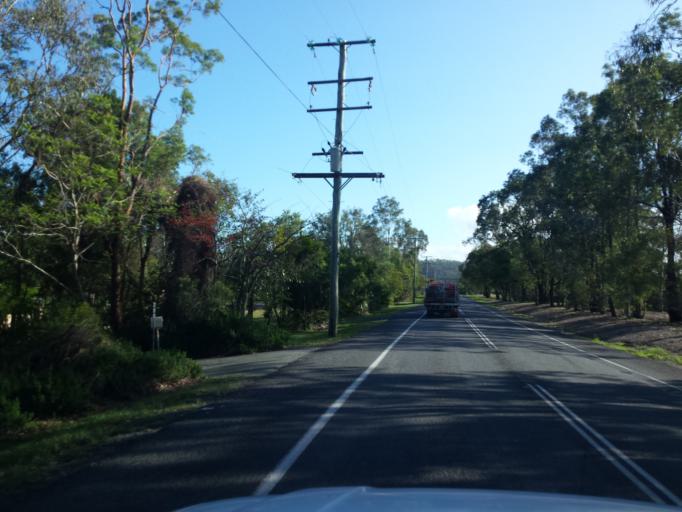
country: AU
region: Queensland
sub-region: Logan
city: Windaroo
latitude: -27.7441
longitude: 153.1869
